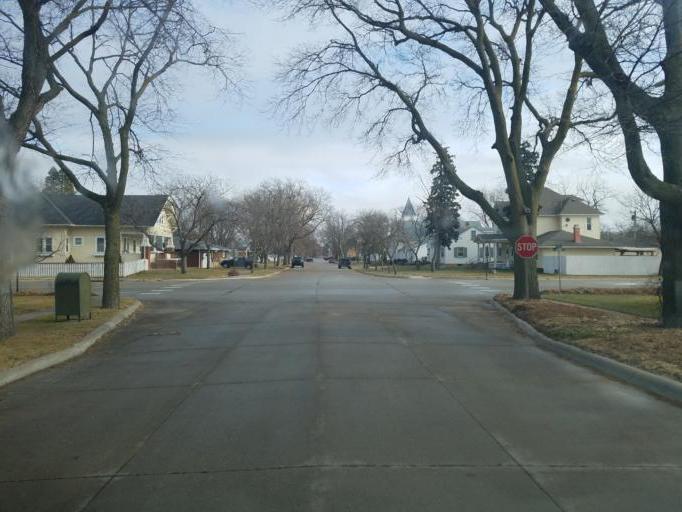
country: US
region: Nebraska
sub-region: Pierce County
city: Pierce
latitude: 42.1971
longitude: -97.5289
